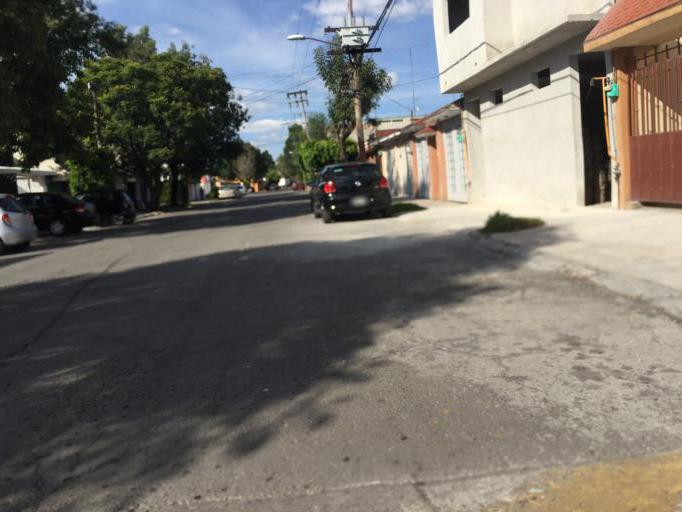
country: MX
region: Mexico
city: Cuautitlan Izcalli
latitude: 19.6671
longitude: -99.2063
